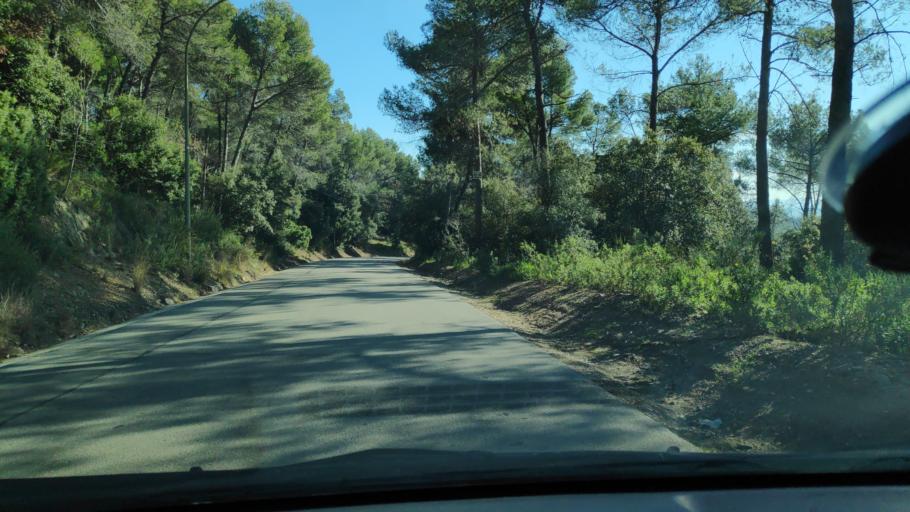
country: ES
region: Catalonia
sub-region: Provincia de Barcelona
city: Matadepera
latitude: 41.5973
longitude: 2.0117
